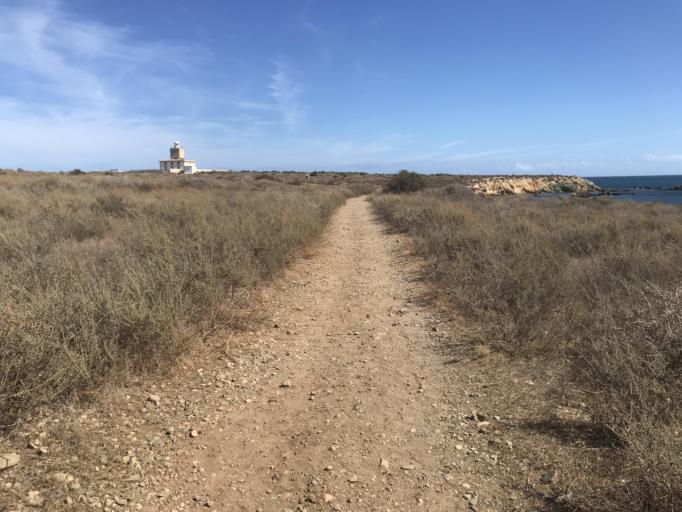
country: ES
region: Valencia
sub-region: Provincia de Alicante
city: Santa Pola
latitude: 38.1633
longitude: -0.4745
